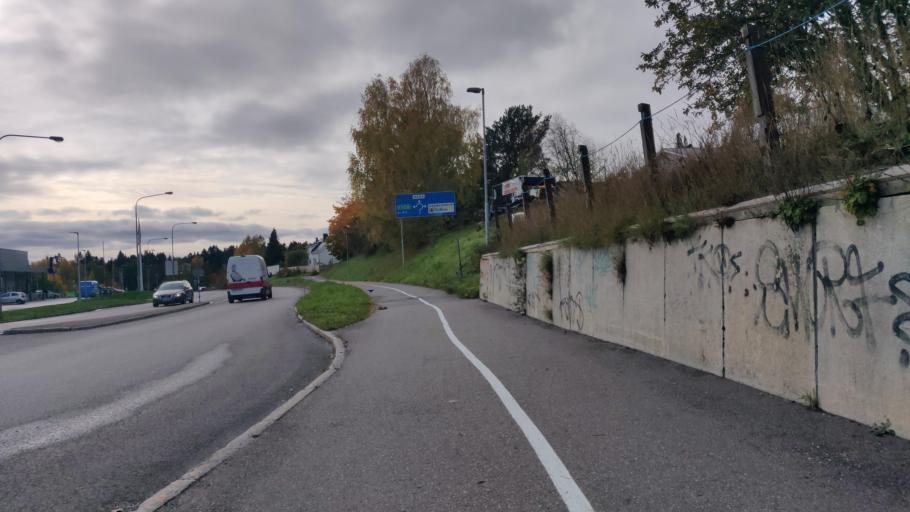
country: SE
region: Vaesternorrland
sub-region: Sundsvalls Kommun
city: Sundsvall
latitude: 62.4131
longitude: 17.3362
